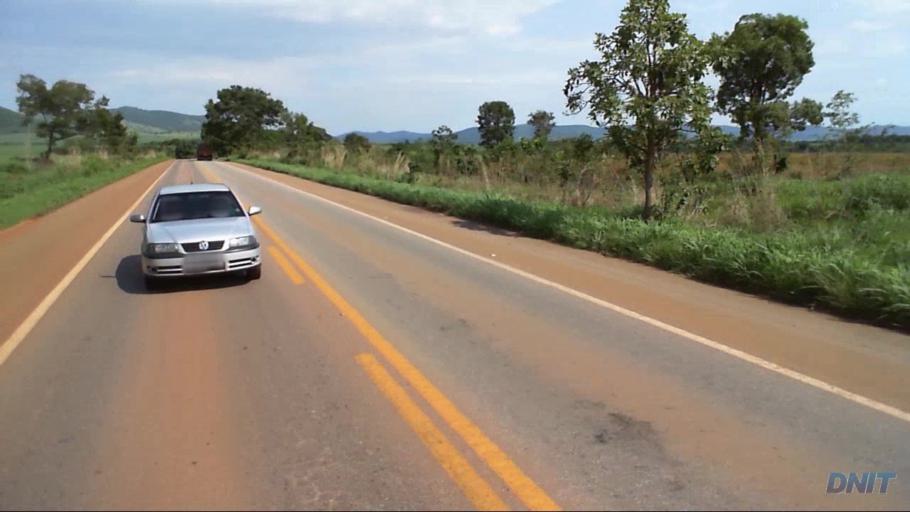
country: BR
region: Goias
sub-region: Barro Alto
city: Barro Alto
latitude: -15.0585
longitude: -48.8787
